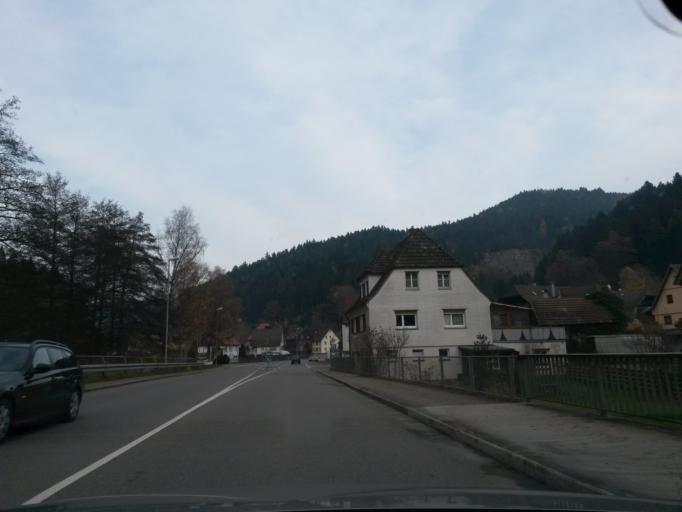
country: DE
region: Baden-Wuerttemberg
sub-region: Karlsruhe Region
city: Alpirsbach
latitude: 48.3293
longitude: 8.3964
